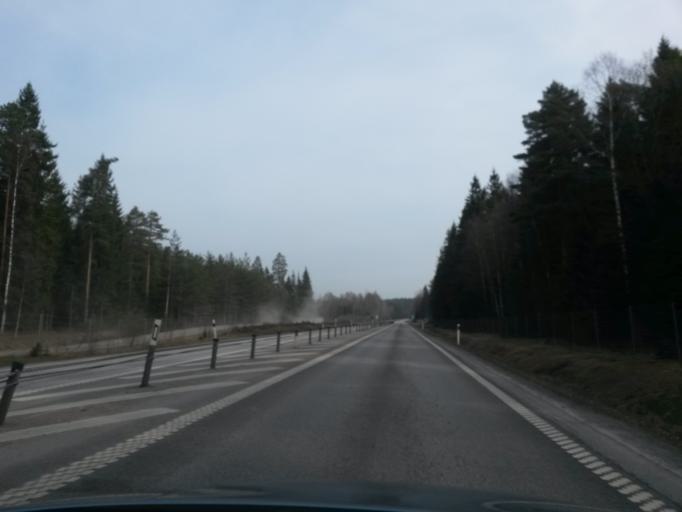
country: SE
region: Vaestra Goetaland
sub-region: Gullspangs Kommun
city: Anderstorp
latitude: 58.9367
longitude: 14.4308
